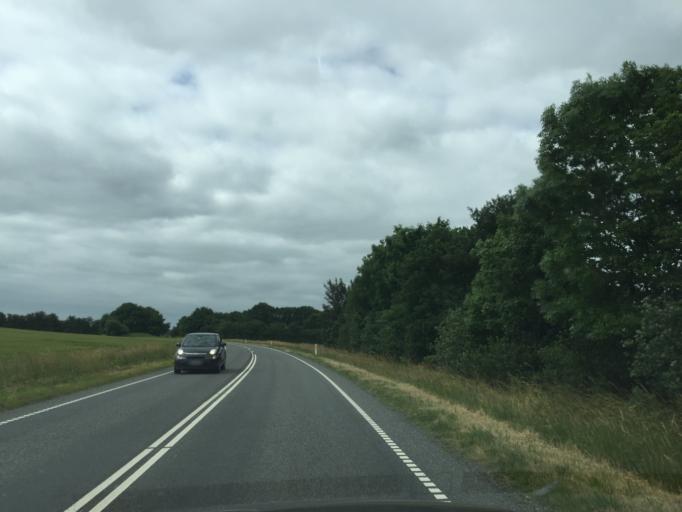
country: DK
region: South Denmark
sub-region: Vejen Kommune
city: Holsted
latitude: 55.4146
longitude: 8.9441
